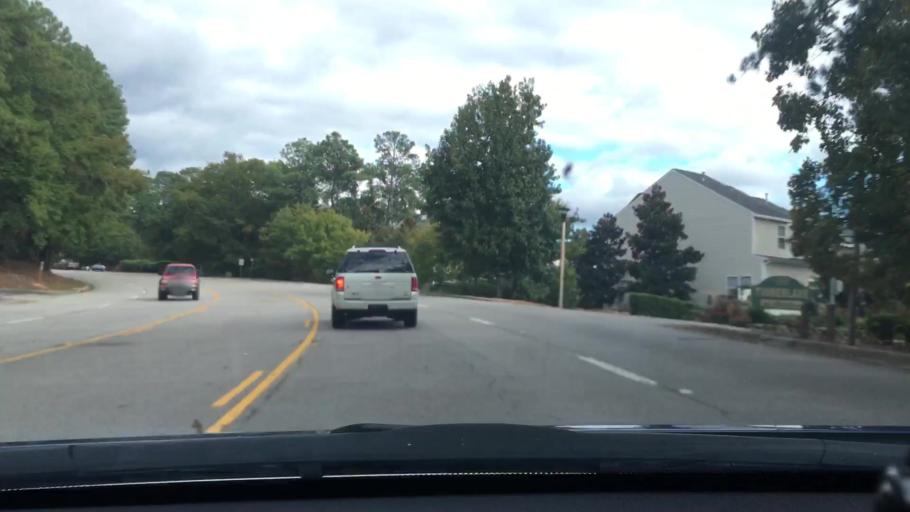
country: US
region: South Carolina
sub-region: Lexington County
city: Seven Oaks
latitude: 34.0803
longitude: -81.1470
